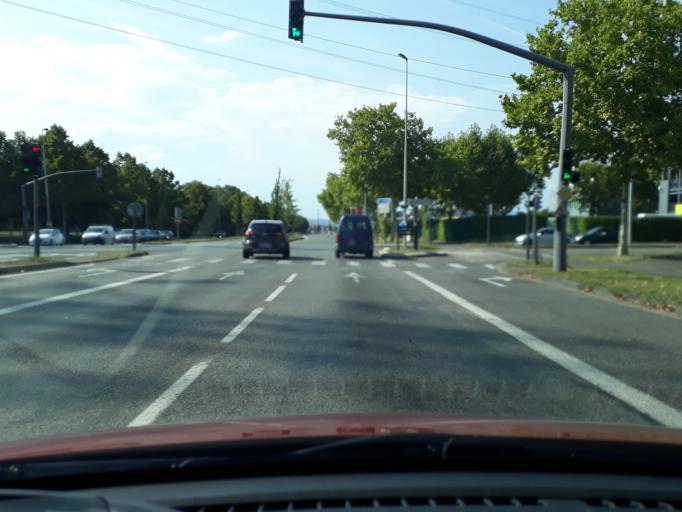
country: FR
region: Rhone-Alpes
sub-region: Departement du Rhone
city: Bron
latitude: 45.7074
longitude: 4.9084
